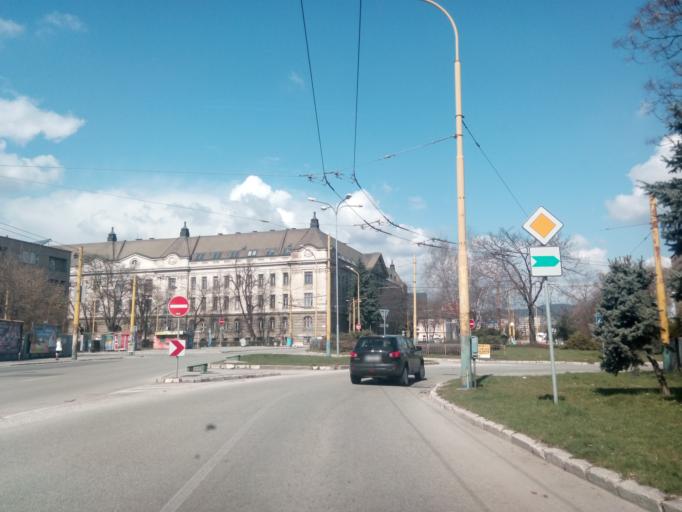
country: SK
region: Kosicky
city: Kosice
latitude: 48.7270
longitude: 21.2578
